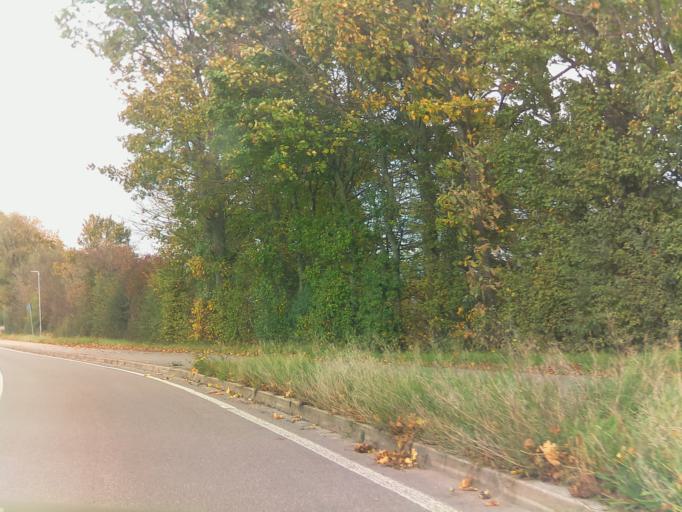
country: DE
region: Baden-Wuerttemberg
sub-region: Karlsruhe Region
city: Weingarten
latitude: 49.0607
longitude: 8.5167
